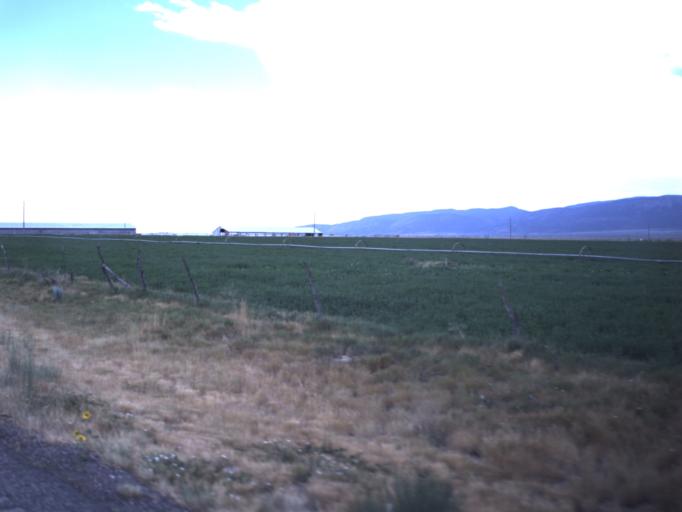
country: US
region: Utah
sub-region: Sanpete County
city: Ephraim
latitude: 39.4343
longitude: -111.5623
